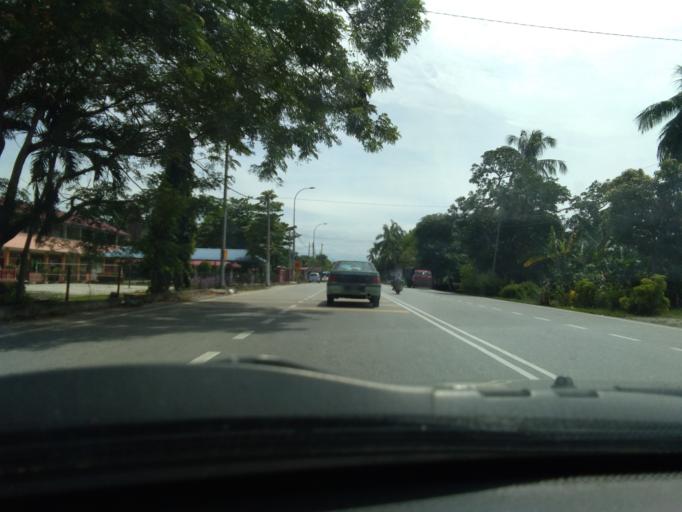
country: MY
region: Perak
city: Bagan Serai
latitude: 5.0322
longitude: 100.5624
